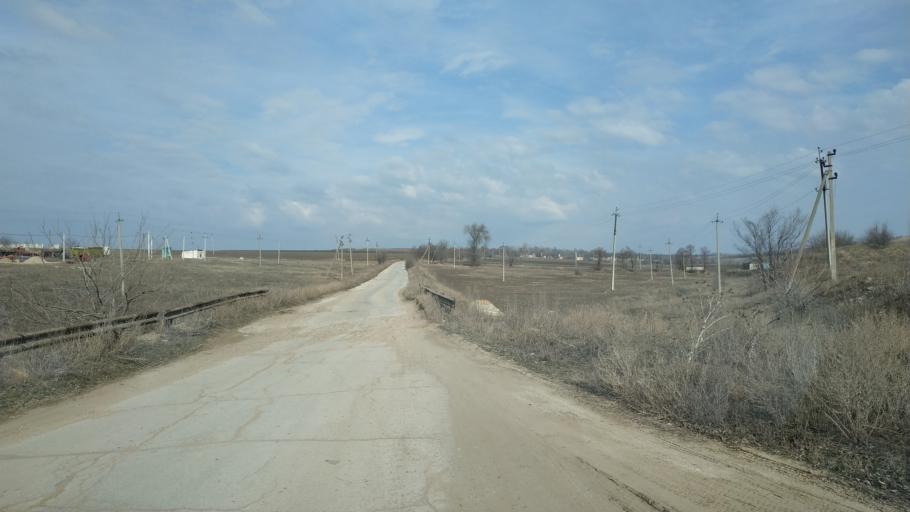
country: MD
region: Anenii Noi
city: Anenii Noi
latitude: 46.9319
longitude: 29.1071
